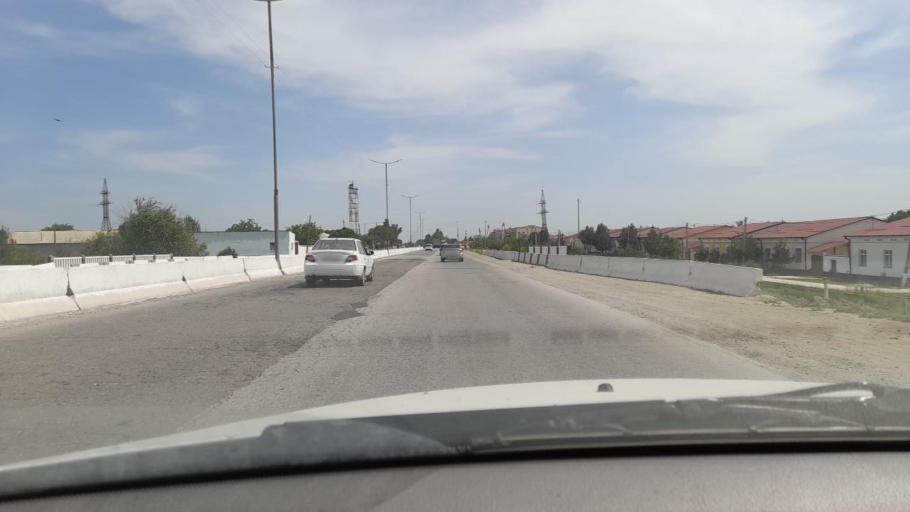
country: UZ
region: Samarqand
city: Oqtosh
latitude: 40.0452
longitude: 65.6681
